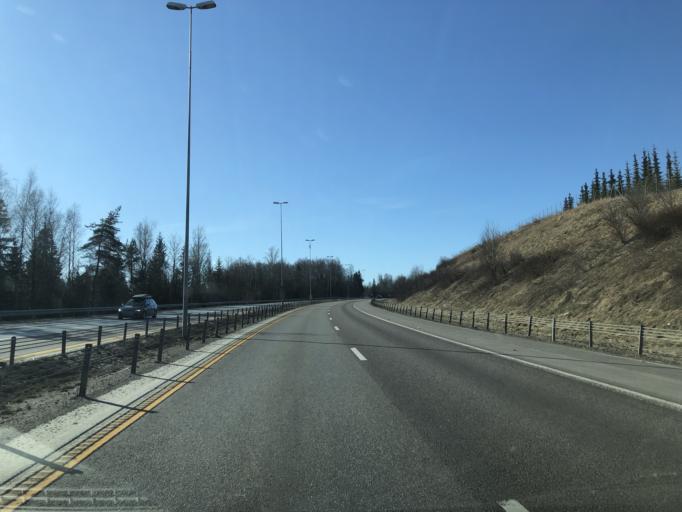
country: NO
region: Akershus
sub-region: Skedsmo
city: Leirsund
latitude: 60.0020
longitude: 11.0455
